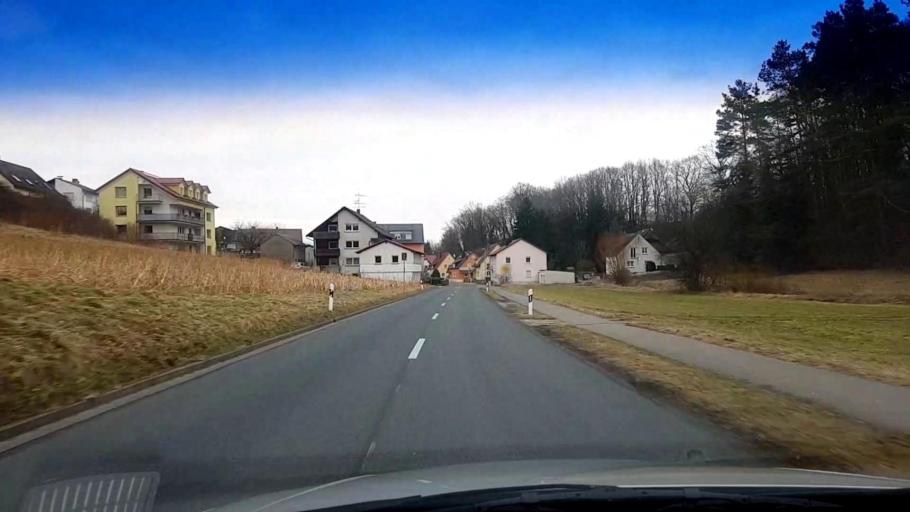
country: DE
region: Bavaria
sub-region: Upper Franconia
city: Bischberg
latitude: 49.9086
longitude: 10.8208
